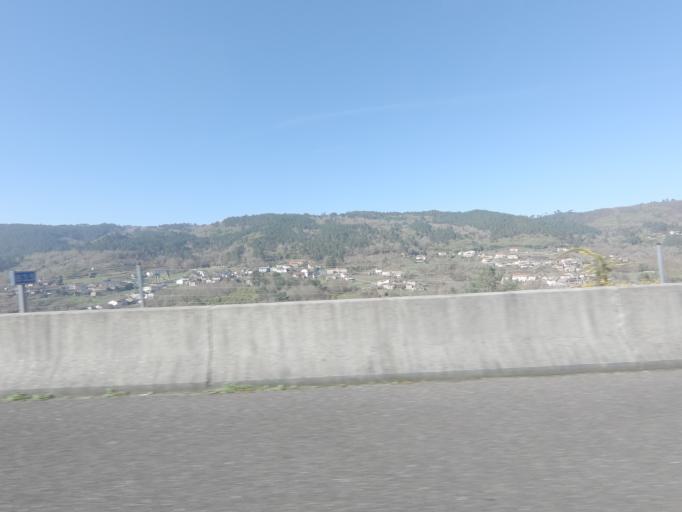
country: ES
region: Galicia
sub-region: Provincia de Ourense
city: Punxin
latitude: 42.3713
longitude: -7.9931
